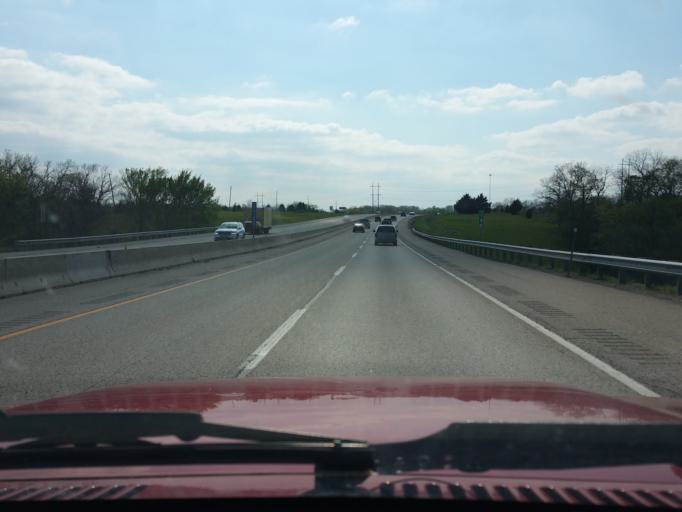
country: US
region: Kansas
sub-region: Douglas County
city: Lawrence
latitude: 38.9973
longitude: -95.3277
